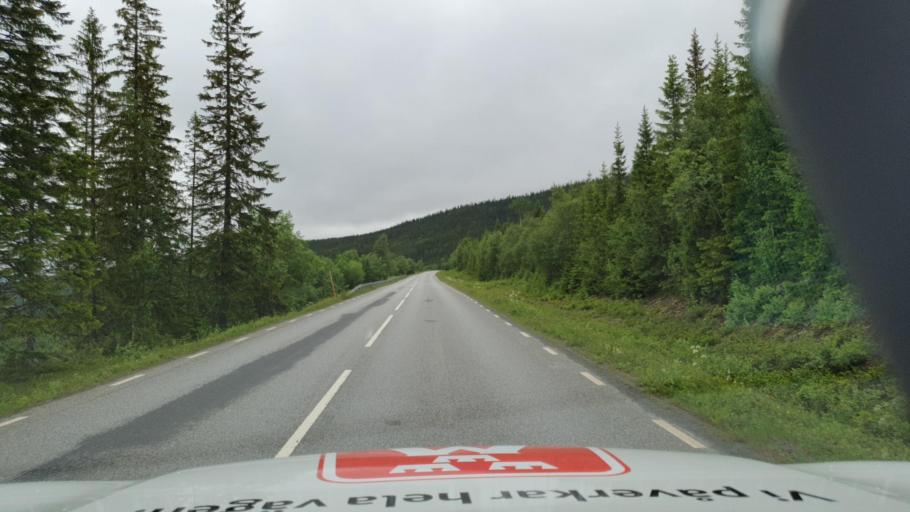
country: SE
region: Jaemtland
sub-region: Are Kommun
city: Are
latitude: 63.4878
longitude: 13.1860
